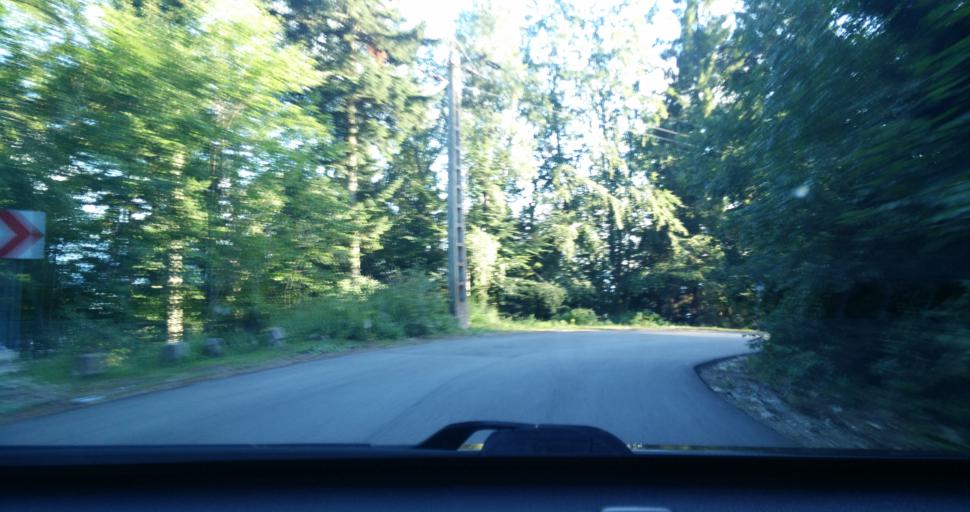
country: RO
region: Bihor
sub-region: Oras Nucet
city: Nucet
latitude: 46.5135
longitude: 22.6341
